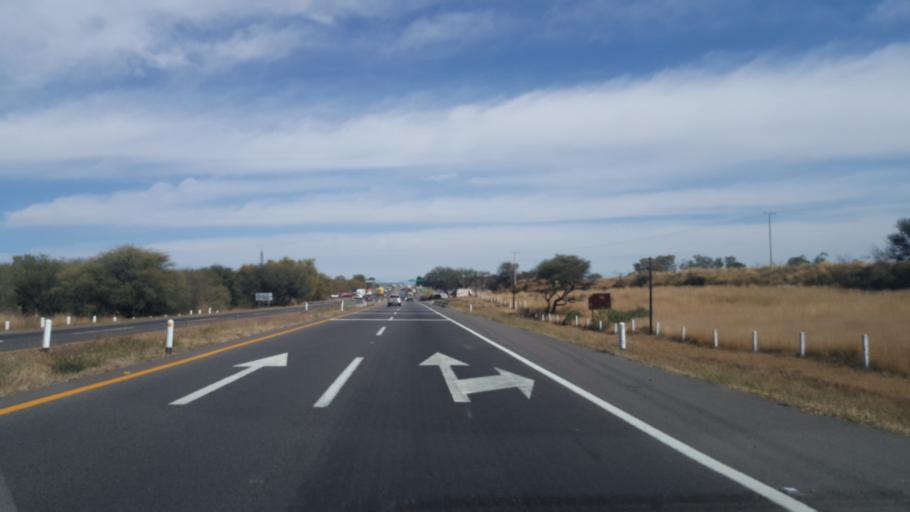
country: MX
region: Jalisco
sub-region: Lagos de Moreno
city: Cristeros [Fraccionamiento]
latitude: 21.3149
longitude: -102.0519
